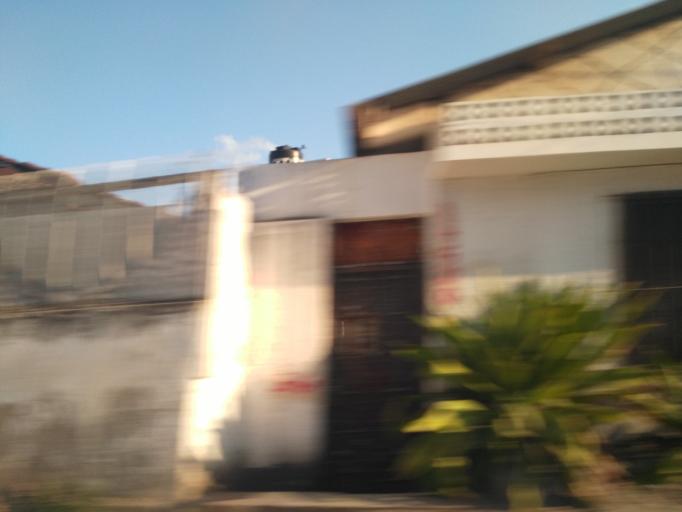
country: TZ
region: Dar es Salaam
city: Magomeni
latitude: -6.7602
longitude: 39.2697
